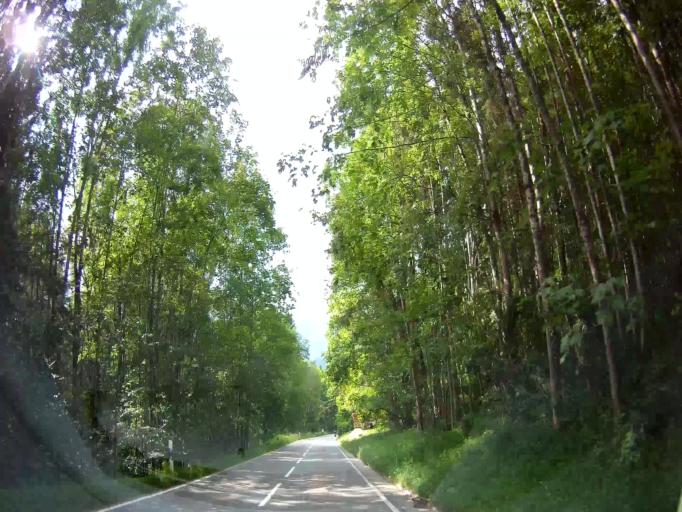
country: DE
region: Bavaria
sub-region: Upper Bavaria
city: Marktschellenberg
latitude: 47.6454
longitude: 13.0594
